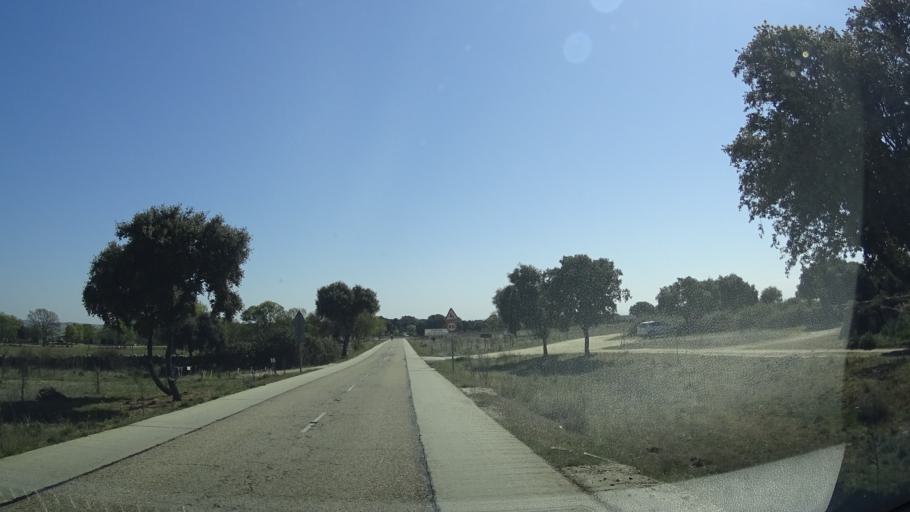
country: ES
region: Madrid
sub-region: Provincia de Madrid
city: Colmenar Viejo
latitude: 40.6444
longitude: -3.8345
